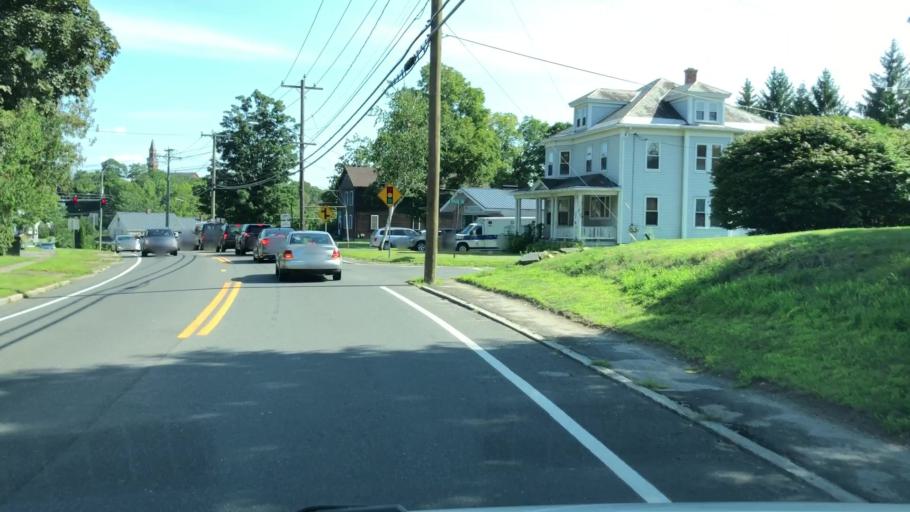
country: US
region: Massachusetts
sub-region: Hampshire County
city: Easthampton
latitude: 42.2756
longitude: -72.6743
